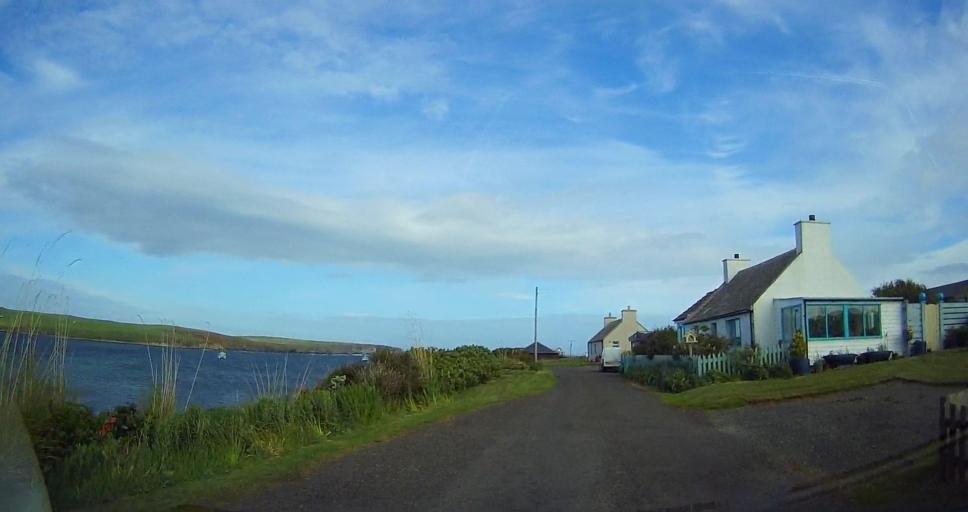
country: GB
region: Scotland
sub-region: Orkney Islands
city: Stromness
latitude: 58.7809
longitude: -3.2336
